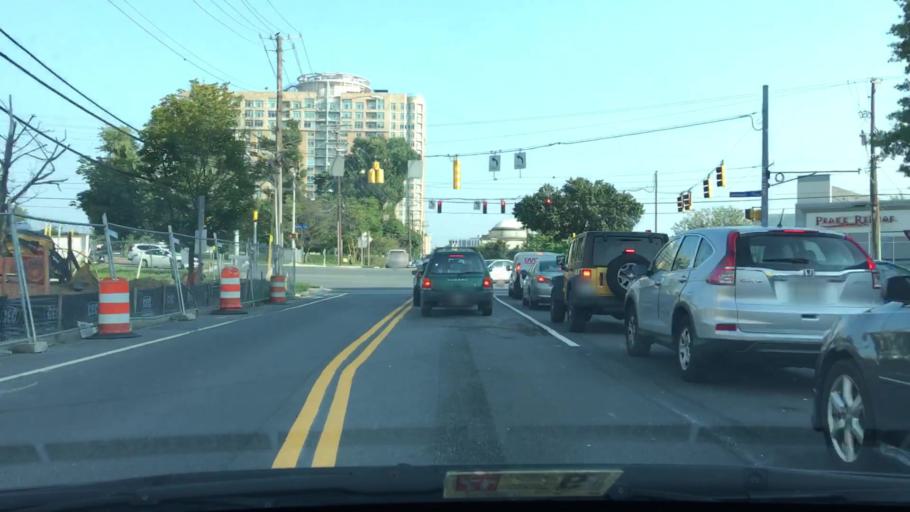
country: US
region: Maryland
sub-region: Montgomery County
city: North Bethesda
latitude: 39.0592
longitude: -77.1194
